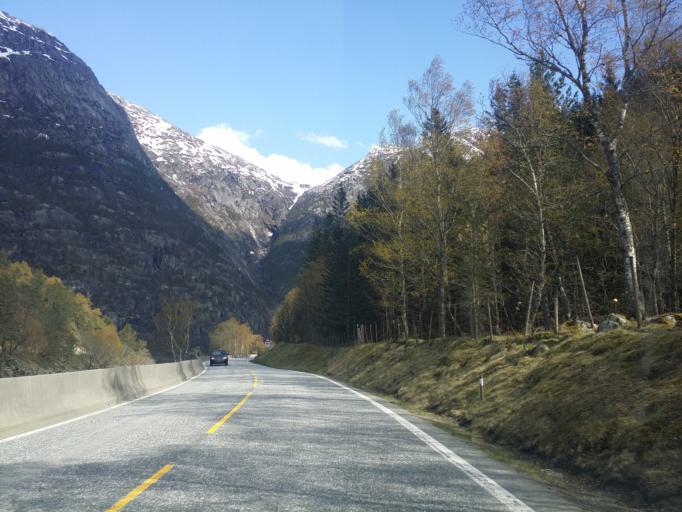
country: NO
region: Hordaland
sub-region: Eidfjord
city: Eidfjord
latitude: 60.4571
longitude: 7.0869
